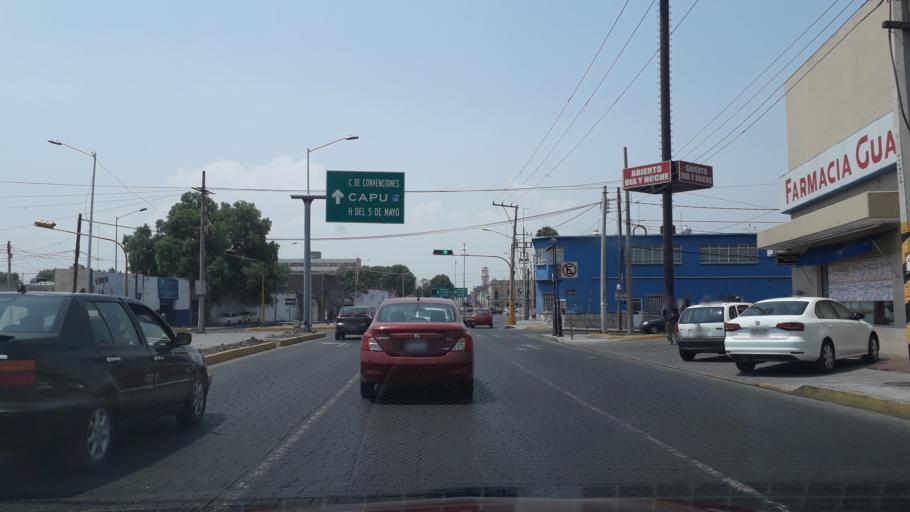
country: MX
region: Puebla
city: Puebla
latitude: 19.0542
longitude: -98.1909
